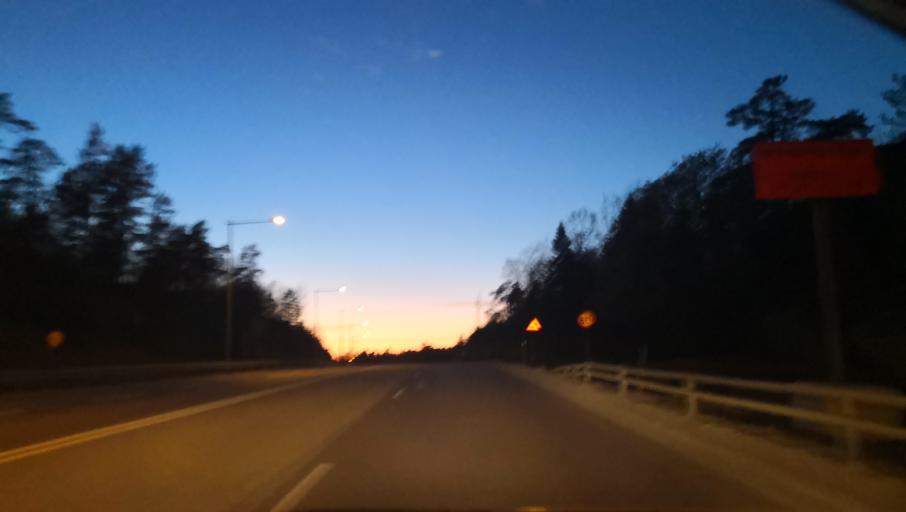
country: SE
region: Stockholm
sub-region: Nynashamns Kommun
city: Nynashamn
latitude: 58.9205
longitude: 17.9511
